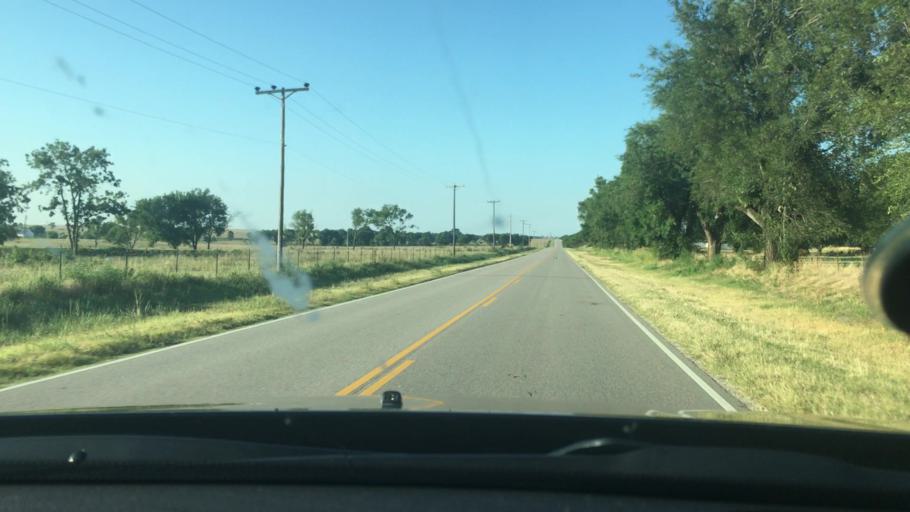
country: US
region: Oklahoma
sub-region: Murray County
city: Sulphur
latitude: 34.6067
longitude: -96.8449
